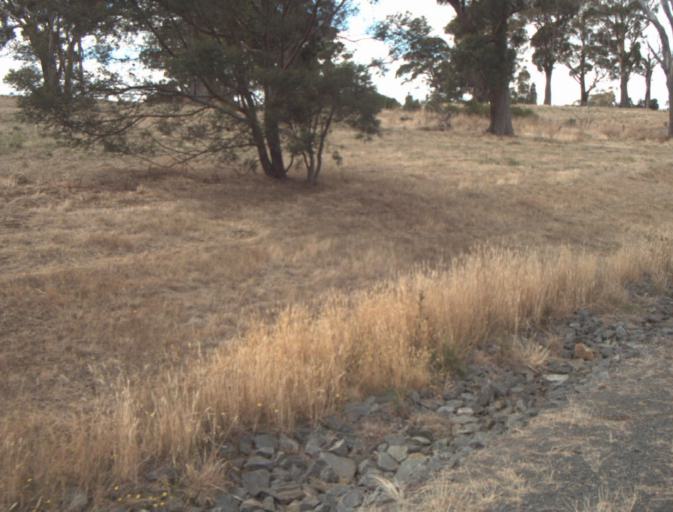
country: AU
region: Tasmania
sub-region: Launceston
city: Mayfield
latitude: -41.3435
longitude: 147.0863
